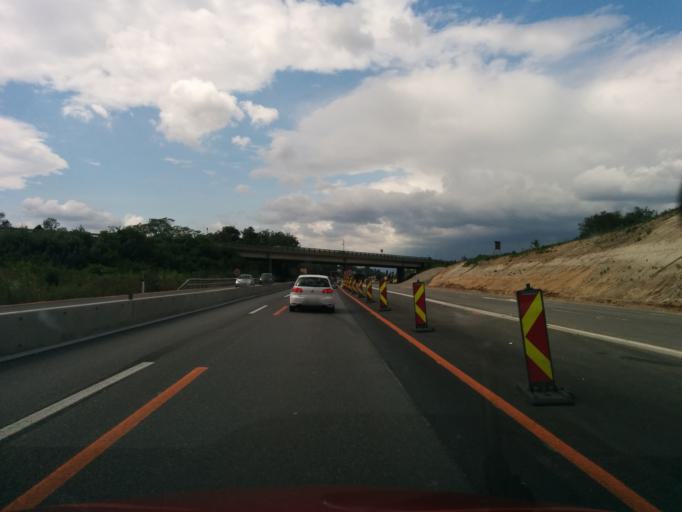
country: AT
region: Lower Austria
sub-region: Politischer Bezirk Wien-Umgebung
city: Rauchenwarth
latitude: 48.1293
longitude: 16.5538
